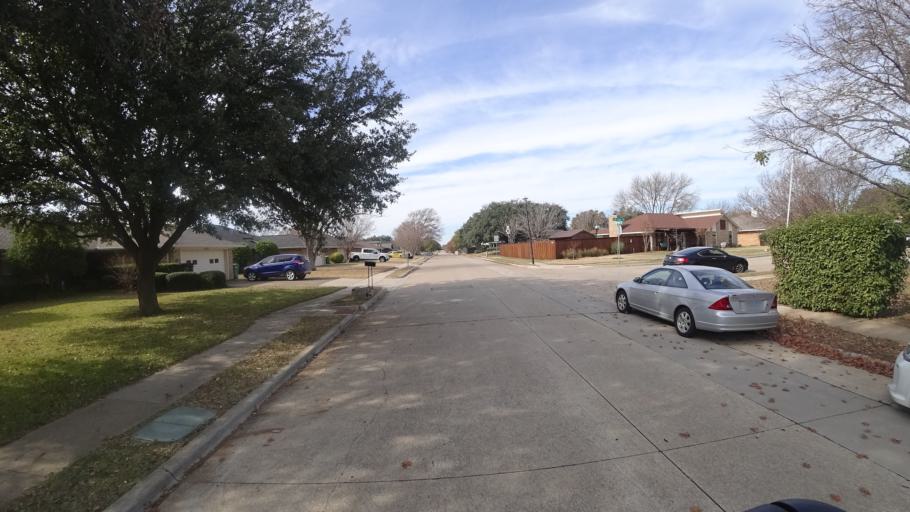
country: US
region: Texas
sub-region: Denton County
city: Highland Village
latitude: 33.0687
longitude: -97.0363
